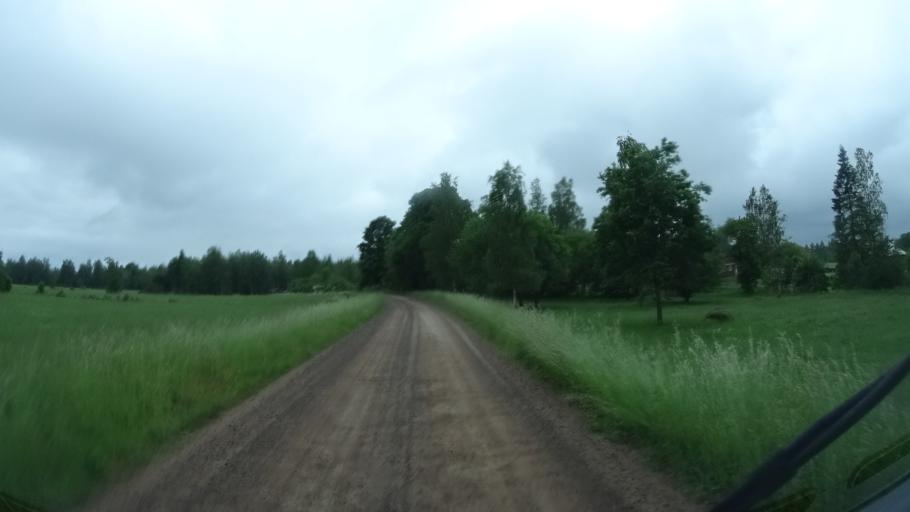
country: SE
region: Joenkoeping
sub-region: Eksjo Kommun
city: Mariannelund
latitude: 57.6203
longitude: 15.6452
